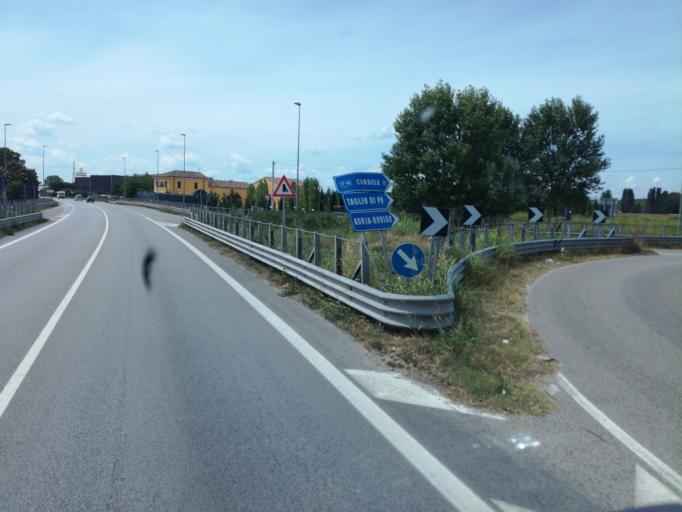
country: IT
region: Veneto
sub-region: Provincia di Rovigo
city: Taglio di Po
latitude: 44.9927
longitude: 12.2210
